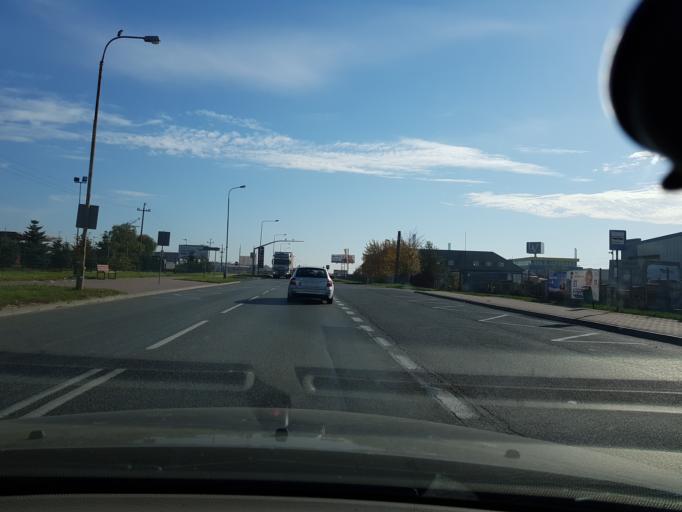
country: PL
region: Lodz Voivodeship
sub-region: Powiat tomaszowski
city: Tomaszow Mazowiecki
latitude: 51.5563
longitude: 20.0202
